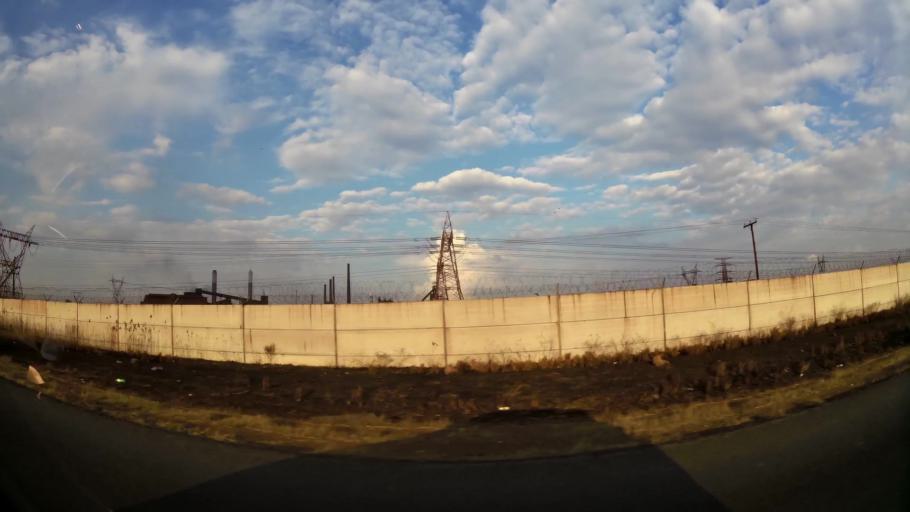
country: ZA
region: Gauteng
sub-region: Sedibeng District Municipality
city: Vanderbijlpark
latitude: -26.6569
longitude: 27.8015
